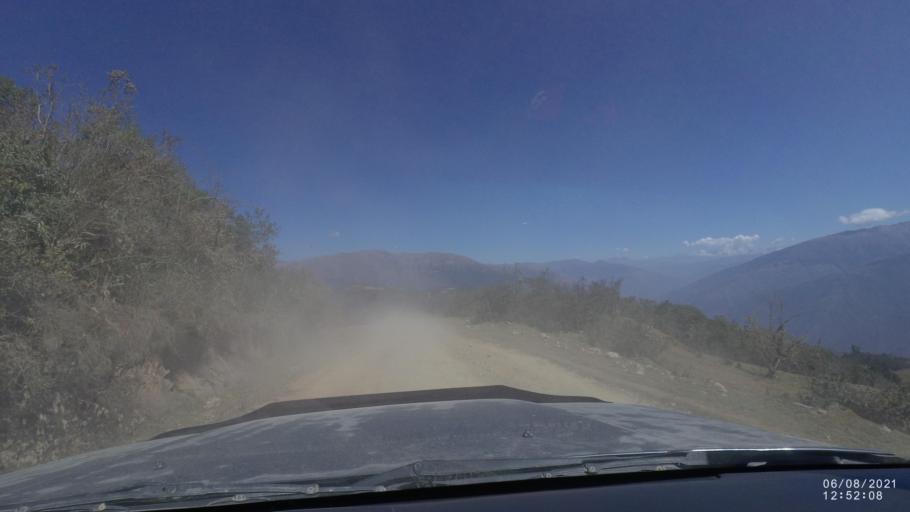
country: BO
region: Cochabamba
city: Colchani
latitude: -16.7628
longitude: -66.6823
